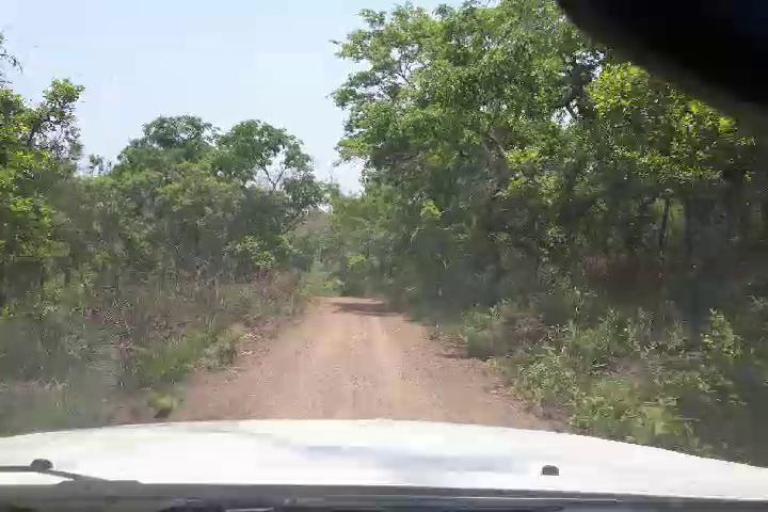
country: SL
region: Northern Province
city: Alikalia
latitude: 9.0792
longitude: -11.4705
